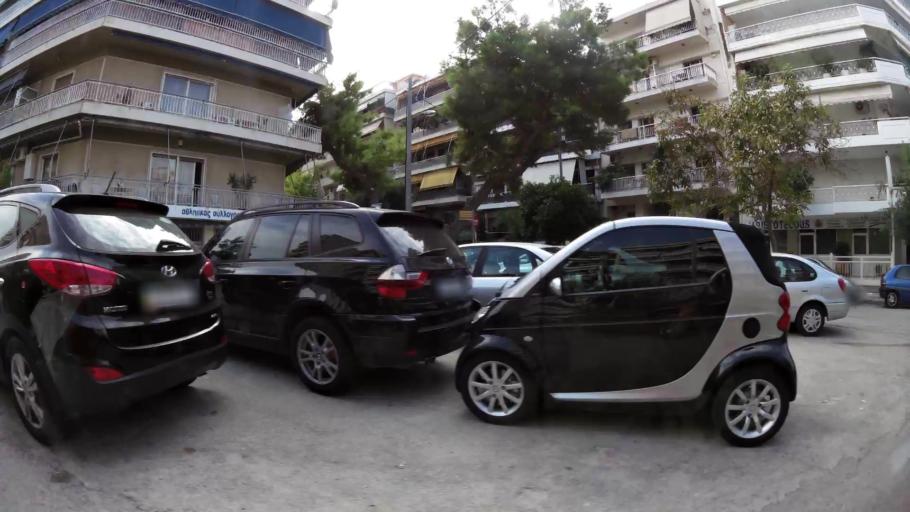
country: GR
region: Attica
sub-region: Nomarchia Athinas
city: Kallithea
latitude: 37.9441
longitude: 23.7034
